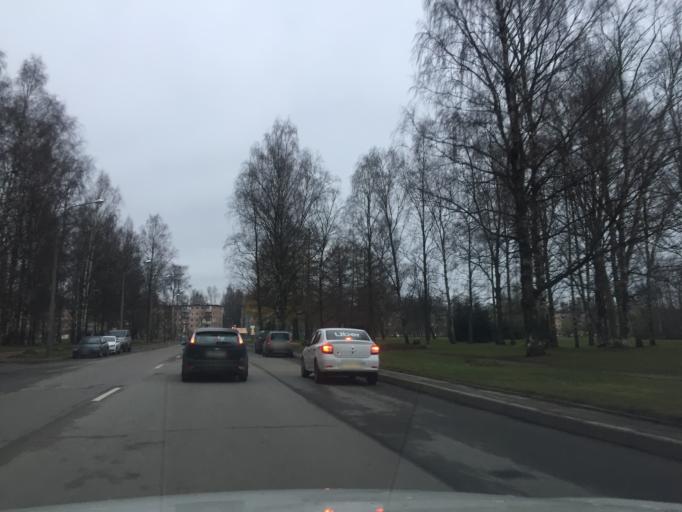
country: RU
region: Leningrad
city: Akademicheskoe
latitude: 60.0197
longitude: 30.3739
